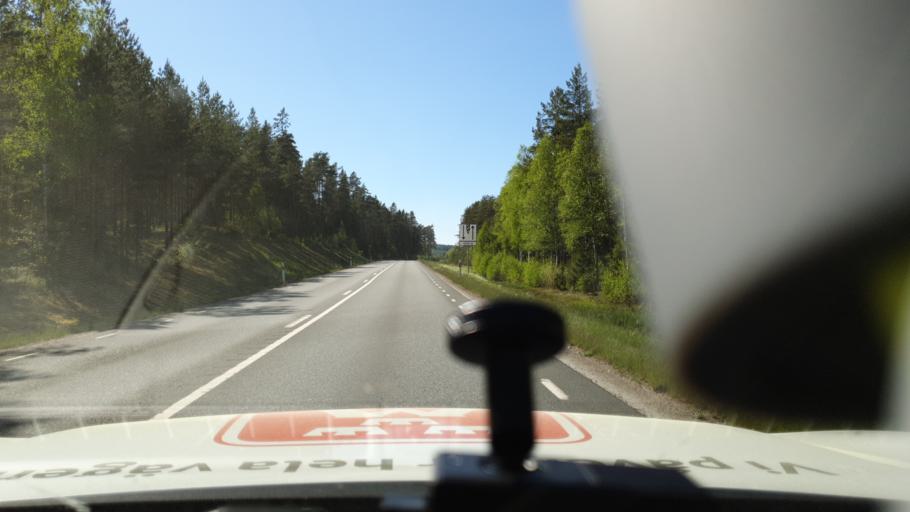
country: SE
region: Joenkoeping
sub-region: Vetlanda Kommun
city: Vetlanda
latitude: 57.4109
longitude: 15.2755
